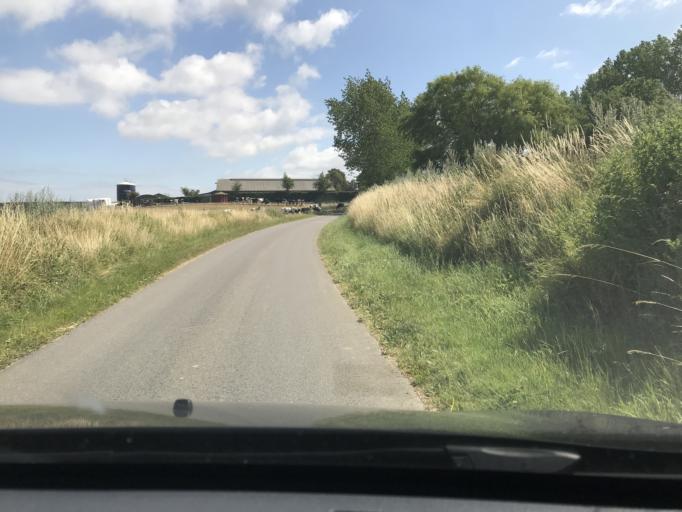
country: DK
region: South Denmark
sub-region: AEro Kommune
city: AEroskobing
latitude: 54.9074
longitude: 10.3015
